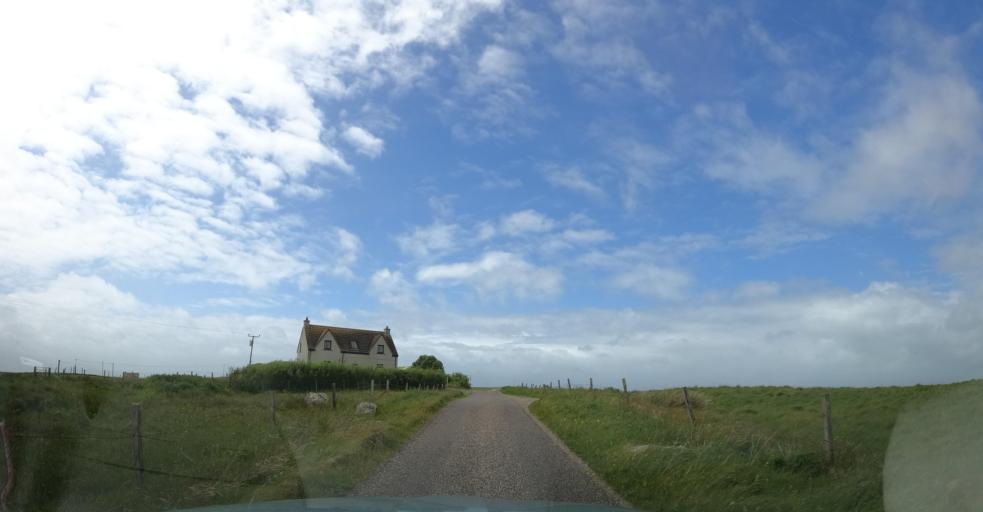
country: GB
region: Scotland
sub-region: Eilean Siar
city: Isle of South Uist
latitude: 57.2730
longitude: -7.4033
